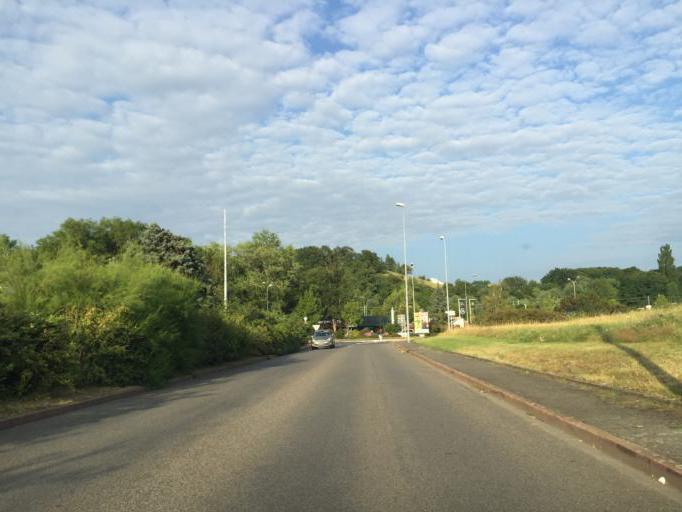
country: FR
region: Auvergne
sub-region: Departement de l'Allier
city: Vichy
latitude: 46.1424
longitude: 3.4138
